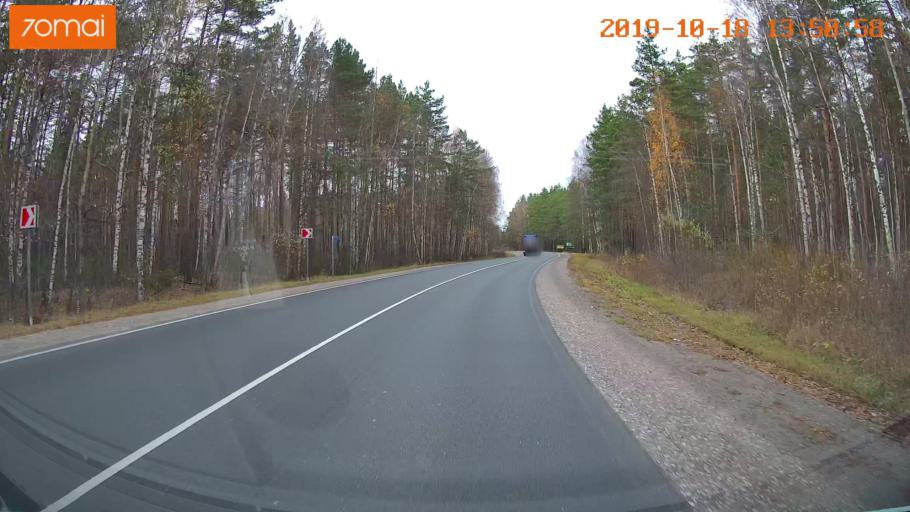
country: RU
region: Moskovskaya
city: Radovitskiy
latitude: 55.0122
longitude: 39.9646
